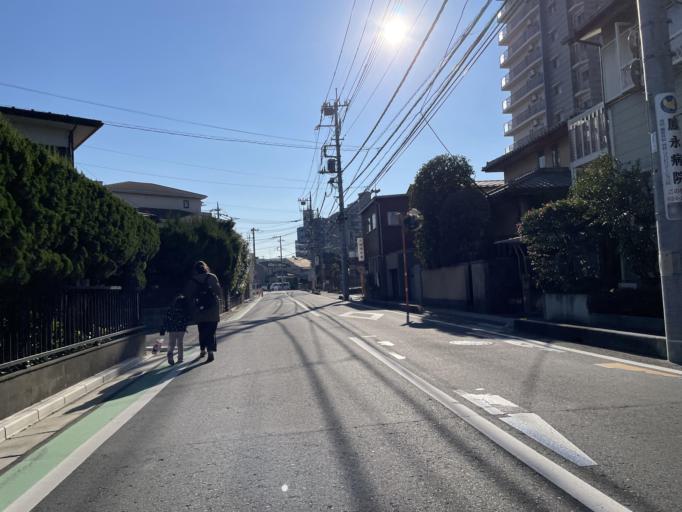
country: JP
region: Saitama
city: Soka
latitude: 35.8092
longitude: 139.8001
